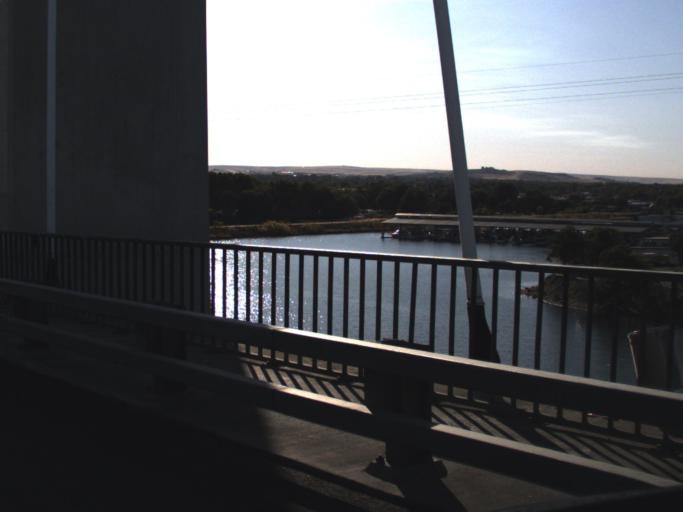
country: US
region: Washington
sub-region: Franklin County
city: Pasco
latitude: 46.2178
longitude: -119.1051
